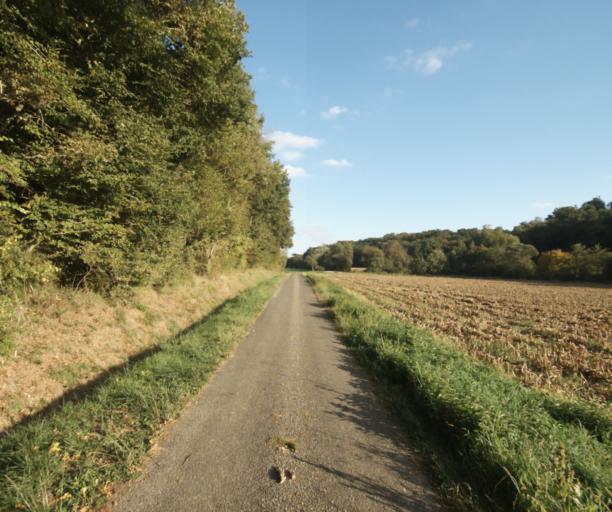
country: FR
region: Midi-Pyrenees
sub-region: Departement du Gers
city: Eauze
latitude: 43.7626
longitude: 0.0926
